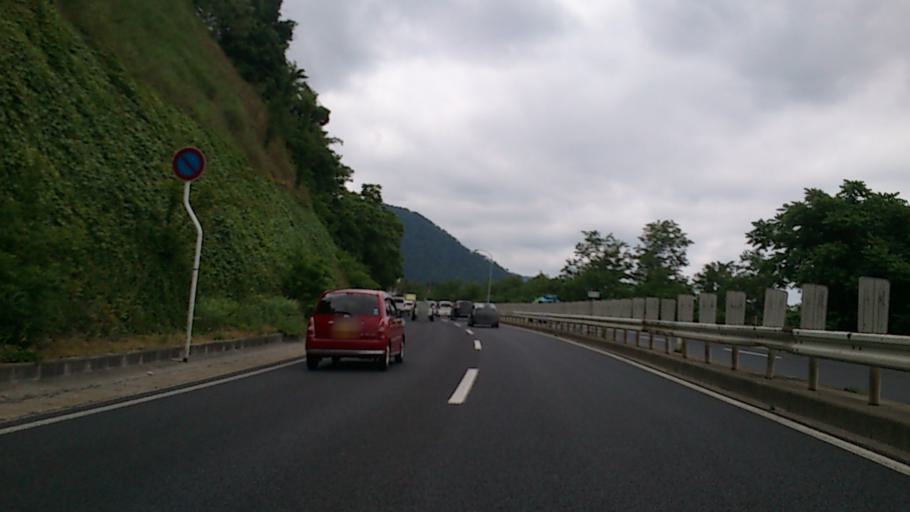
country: JP
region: Yamagata
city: Yamagata-shi
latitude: 38.2535
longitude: 140.3547
